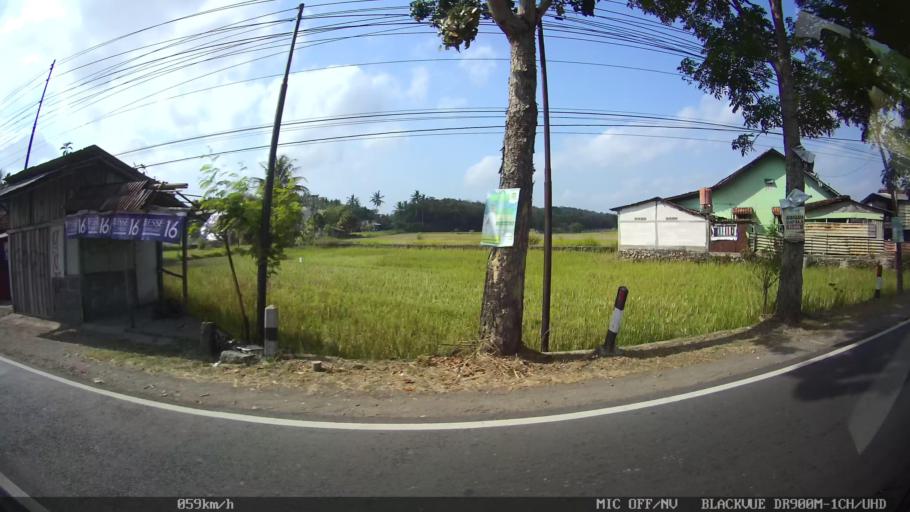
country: ID
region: Daerah Istimewa Yogyakarta
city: Godean
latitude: -7.8192
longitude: 110.2432
